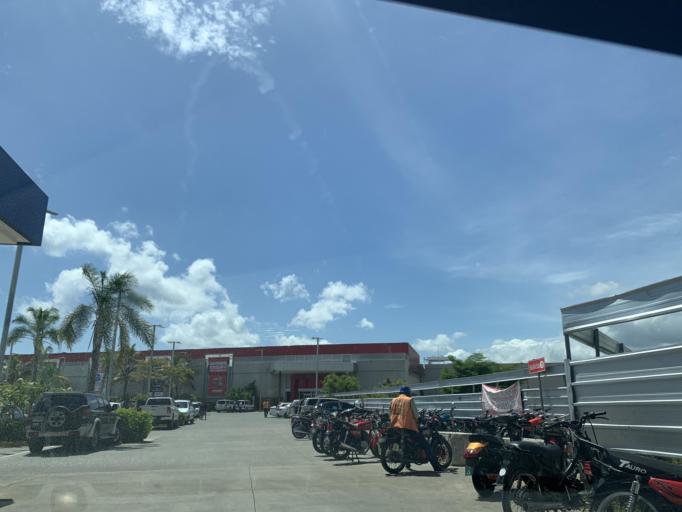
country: DO
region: Puerto Plata
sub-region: Puerto Plata
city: Puerto Plata
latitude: 19.7820
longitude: -70.6742
